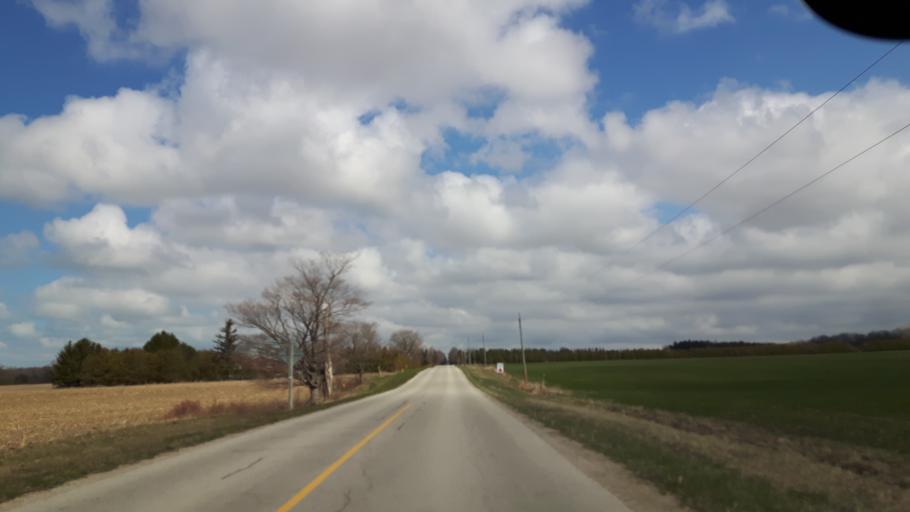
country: CA
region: Ontario
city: Goderich
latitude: 43.6455
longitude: -81.6845
